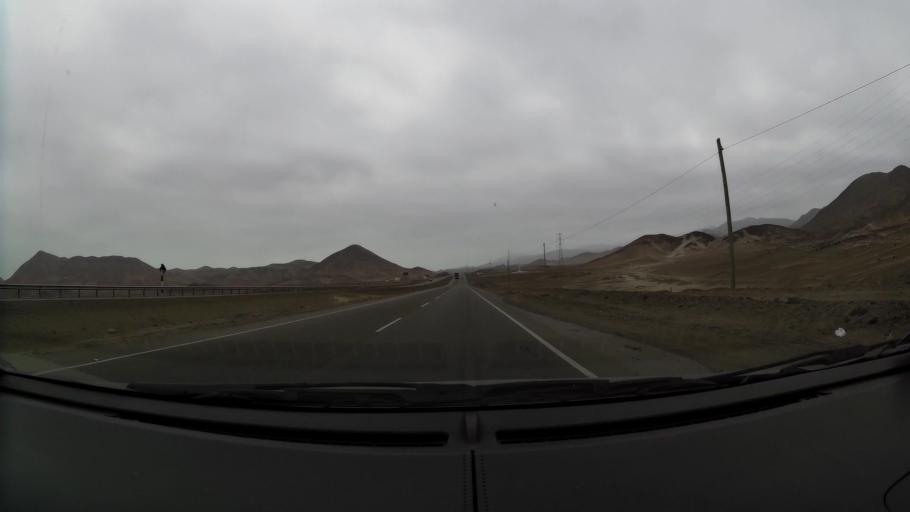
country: PE
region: Lima
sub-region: Barranca
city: Paramonga
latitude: -10.4612
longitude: -77.9175
